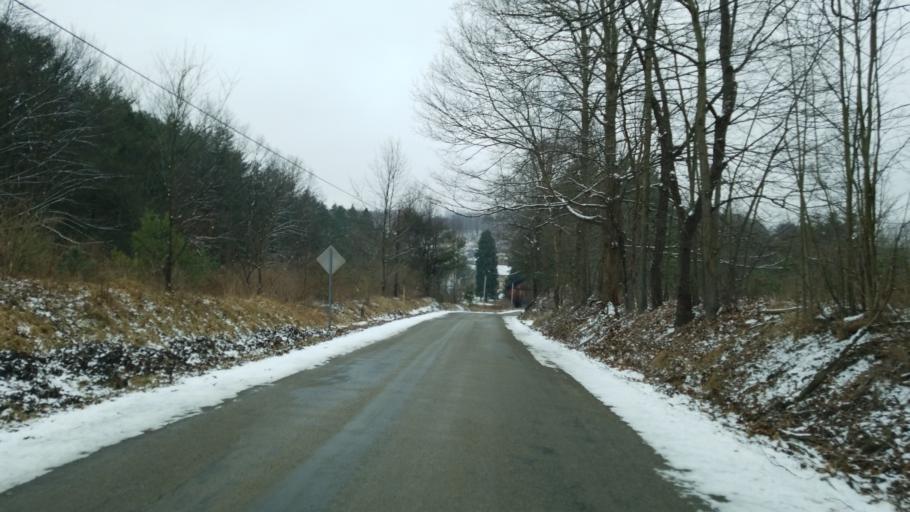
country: US
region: Pennsylvania
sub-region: Jefferson County
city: Reynoldsville
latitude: 41.0877
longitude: -78.8563
